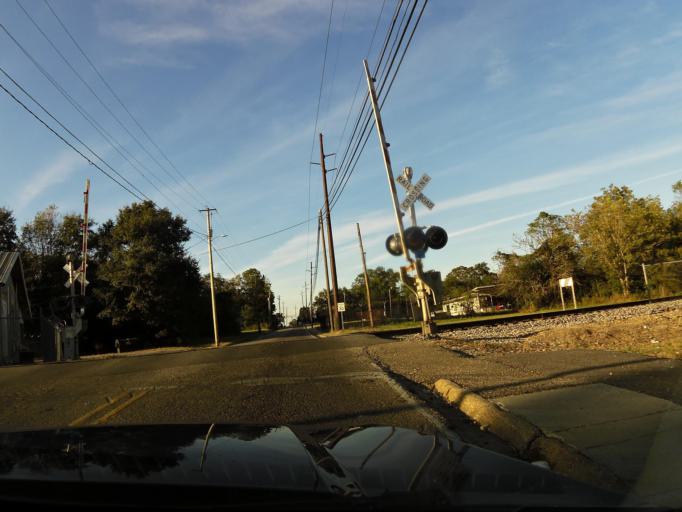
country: US
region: Alabama
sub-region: Houston County
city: Dothan
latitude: 31.2321
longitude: -85.3830
